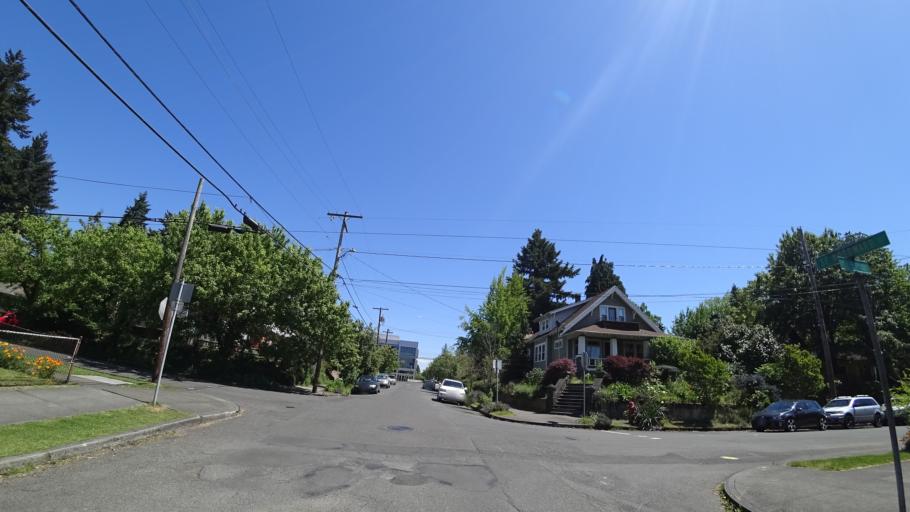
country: US
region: Oregon
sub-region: Multnomah County
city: Lents
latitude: 45.5016
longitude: -122.6102
